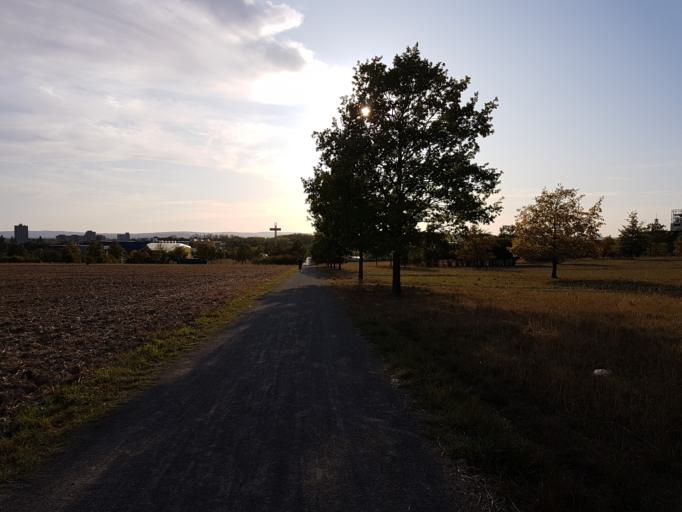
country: DE
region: Lower Saxony
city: Laatzen
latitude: 52.3171
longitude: 9.8258
